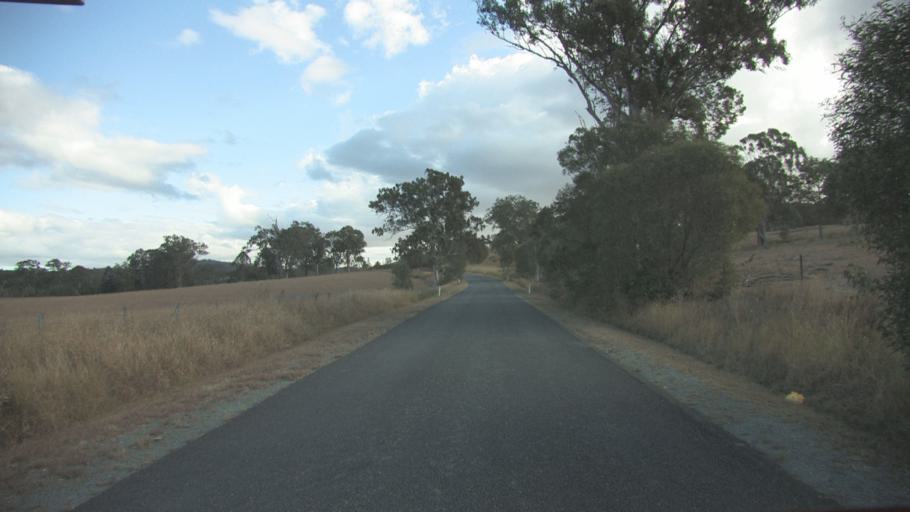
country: AU
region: Queensland
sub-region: Logan
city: Cedar Vale
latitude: -27.8902
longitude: 153.0674
